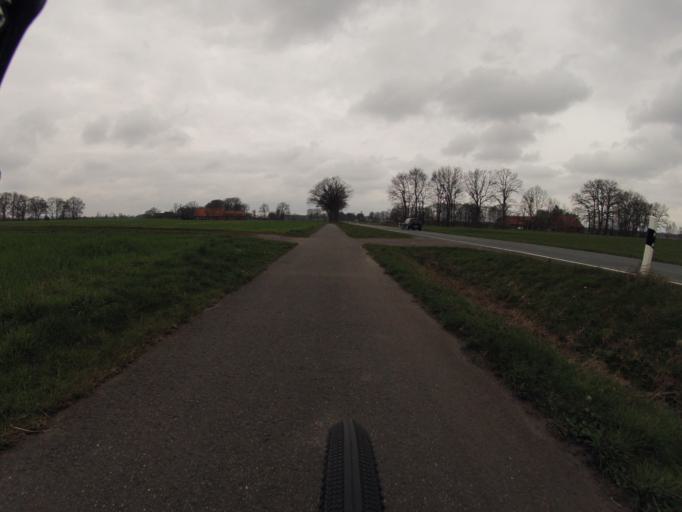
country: DE
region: North Rhine-Westphalia
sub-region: Regierungsbezirk Munster
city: Mettingen
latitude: 52.3452
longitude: 7.8071
